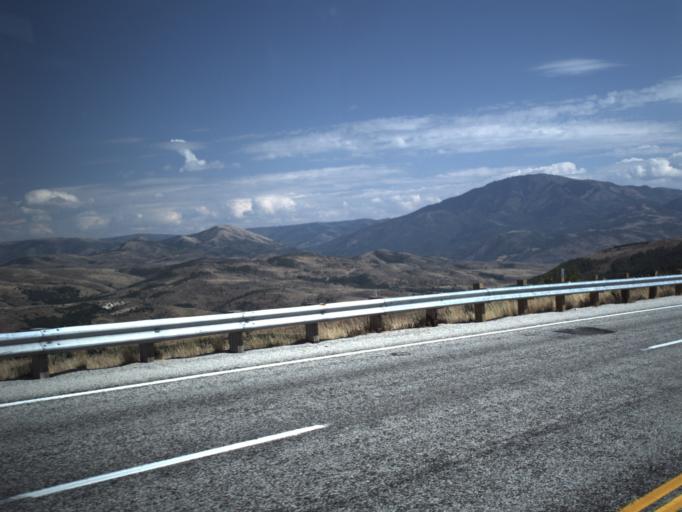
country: US
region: Utah
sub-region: Morgan County
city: Mountain Green
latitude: 41.1922
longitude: -111.8131
